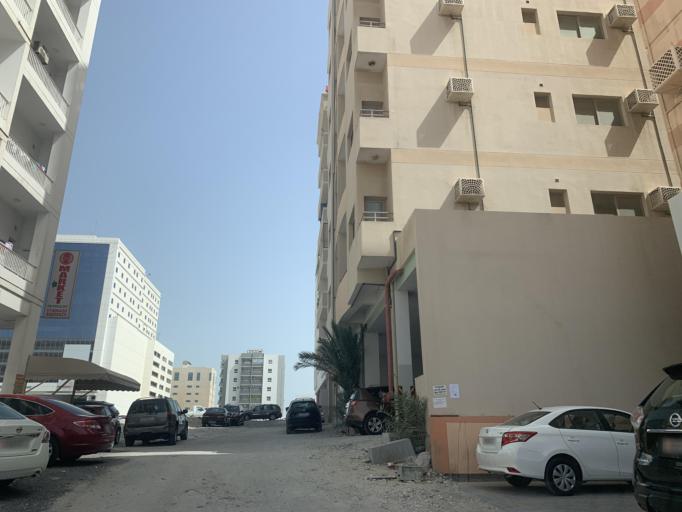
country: BH
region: Northern
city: Madinat `Isa
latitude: 26.1548
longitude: 50.5671
